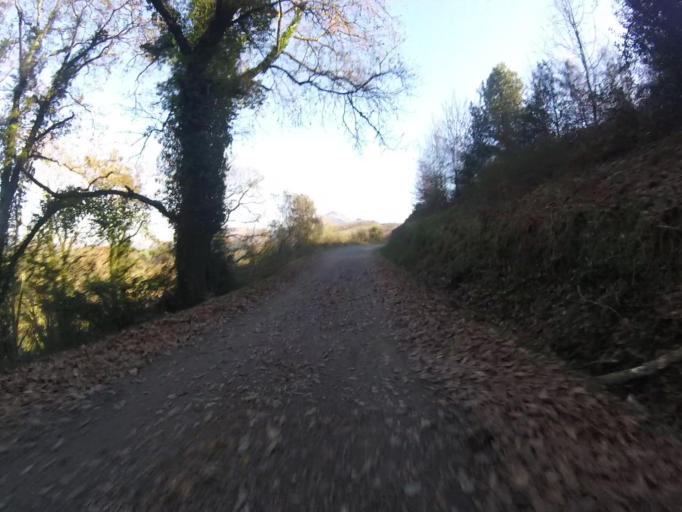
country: ES
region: Navarre
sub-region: Provincia de Navarra
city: Bera
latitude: 43.3175
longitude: -1.6912
